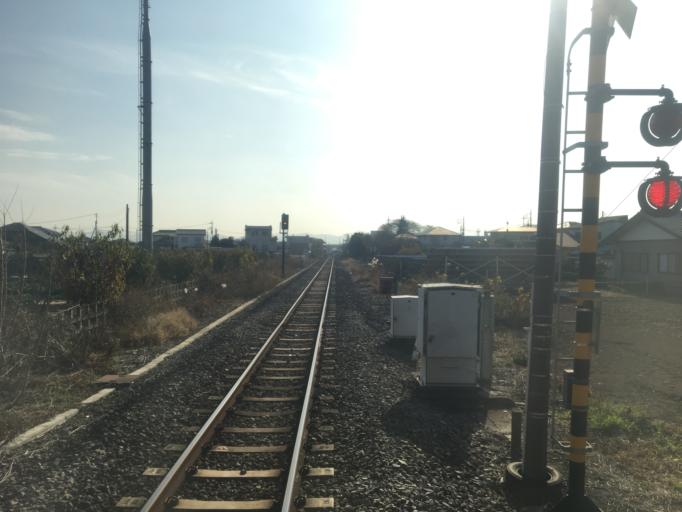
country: JP
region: Gunma
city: Fujioka
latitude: 36.2573
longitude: 139.0835
